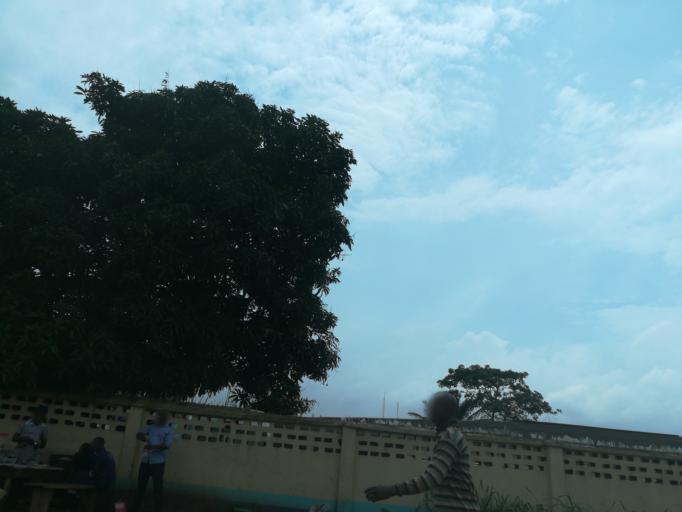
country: NG
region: Lagos
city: Oshodi
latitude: 6.5651
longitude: 3.3221
